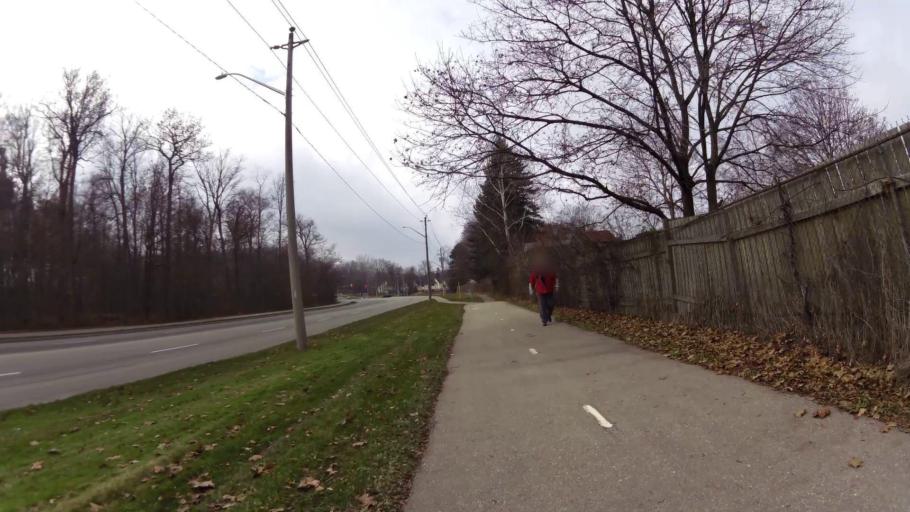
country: CA
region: Ontario
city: Kitchener
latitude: 43.4169
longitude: -80.4777
